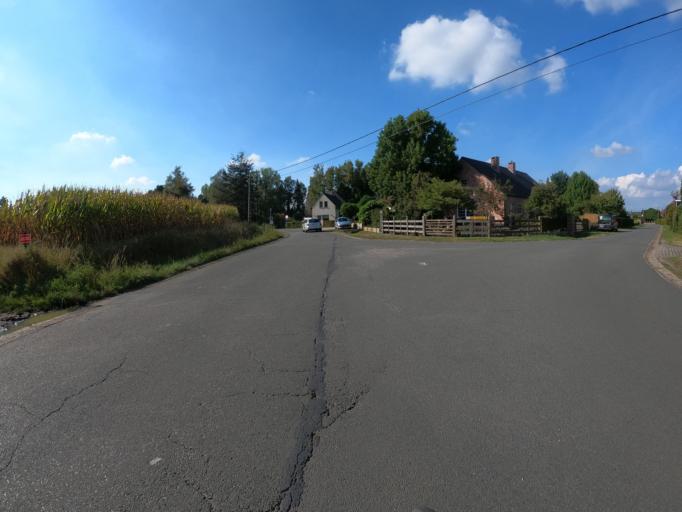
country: BE
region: Flanders
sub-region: Provincie Antwerpen
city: Berlaar
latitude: 51.0764
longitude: 4.6733
